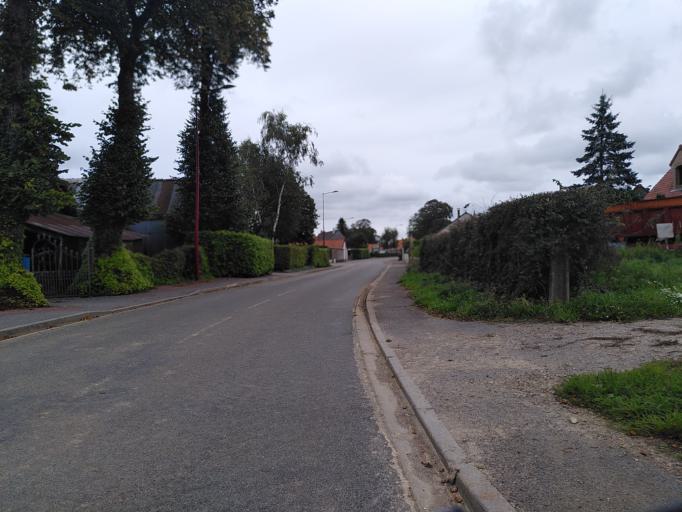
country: FR
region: Nord-Pas-de-Calais
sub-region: Departement du Pas-de-Calais
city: Desvres
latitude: 50.6631
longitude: 1.8993
